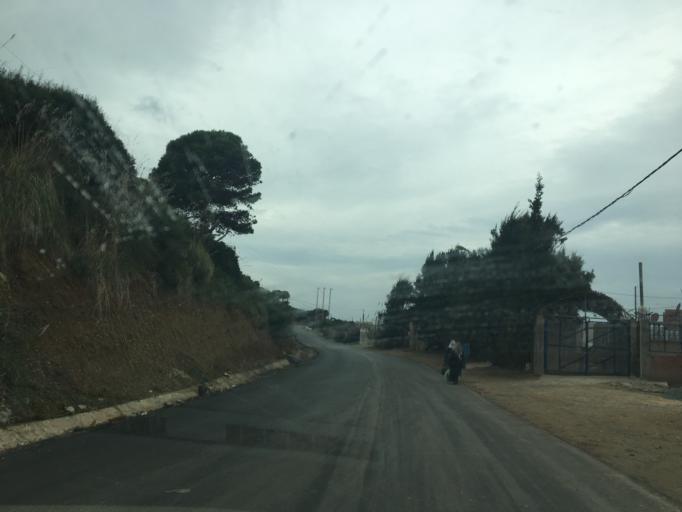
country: DZ
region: Tipaza
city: Tipasa
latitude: 36.6396
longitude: 2.3367
